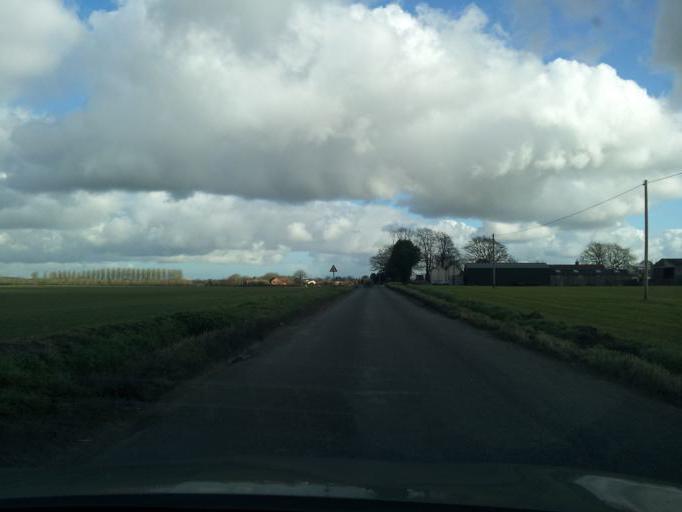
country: GB
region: England
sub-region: Norfolk
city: Mattishall
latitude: 52.6594
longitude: 1.0494
